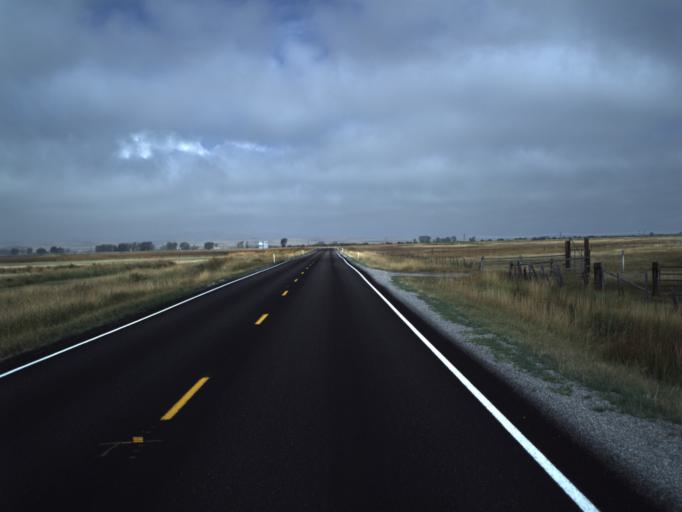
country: US
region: Utah
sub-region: Rich County
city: Randolph
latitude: 41.5045
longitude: -111.1252
